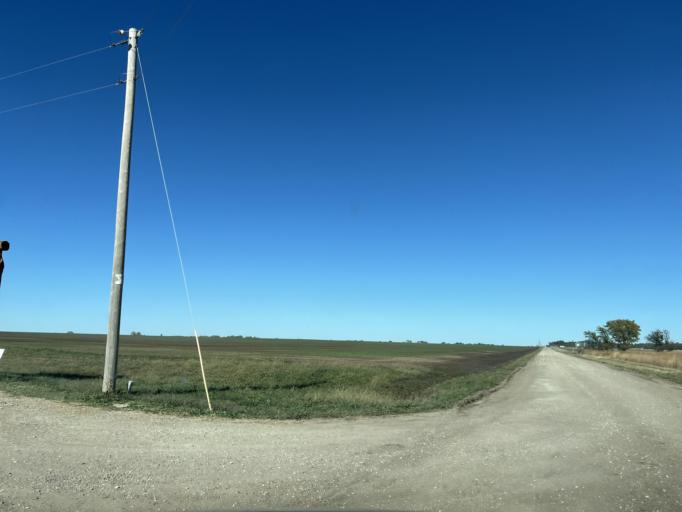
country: US
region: Kansas
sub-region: McPherson County
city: Moundridge
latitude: 38.2231
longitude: -97.6291
